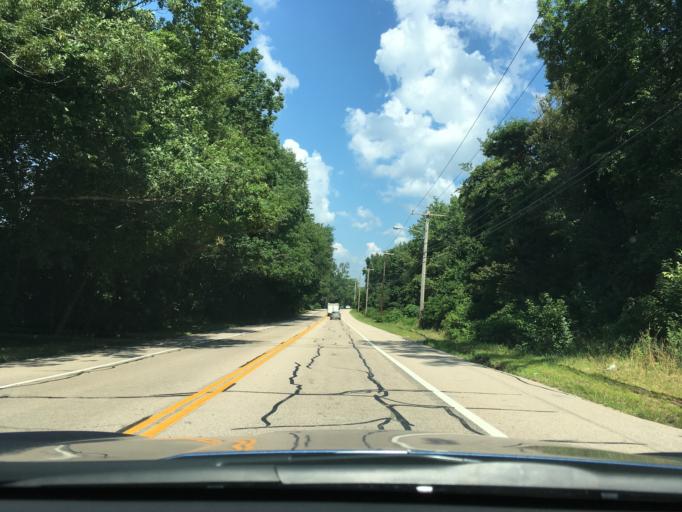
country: US
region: Rhode Island
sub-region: Kent County
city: East Greenwich
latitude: 41.6349
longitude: -71.4939
